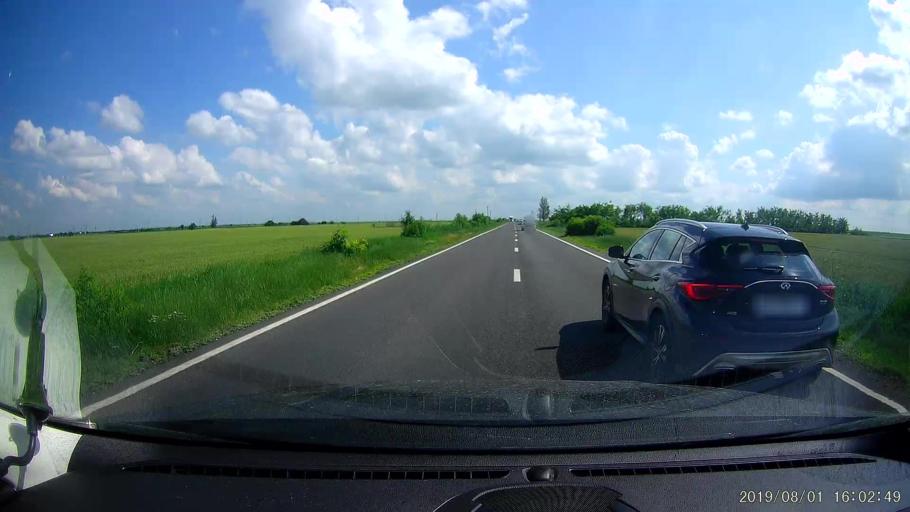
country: RO
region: Calarasi
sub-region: Comuna Dragalina
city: Drajna Noua
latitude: 44.4833
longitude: 27.3863
